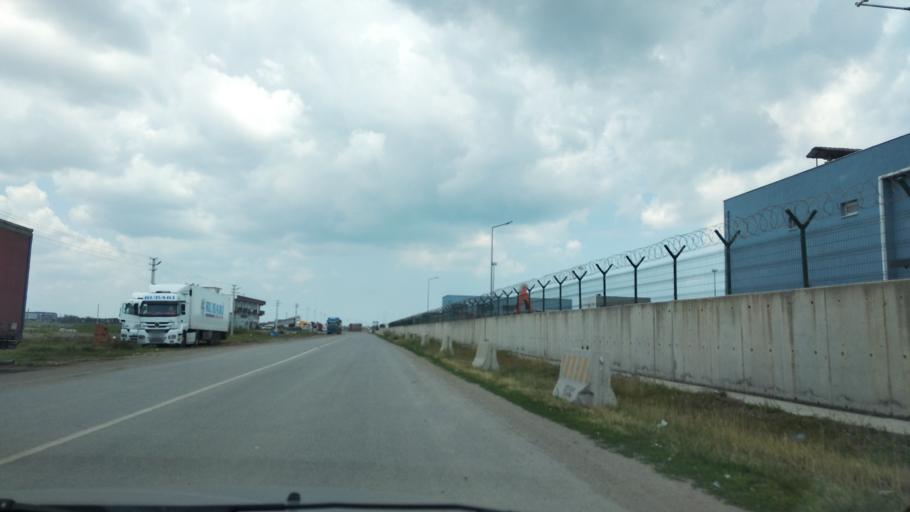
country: TR
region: Sakarya
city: Karasu
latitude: 41.1177
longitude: 30.6726
